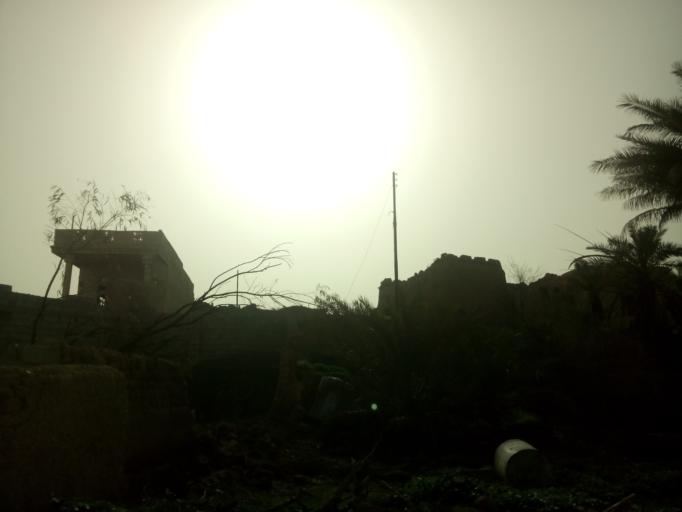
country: IQ
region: Salah ad Din Governorate
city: Tozkhurmato
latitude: 34.7798
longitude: 44.5749
